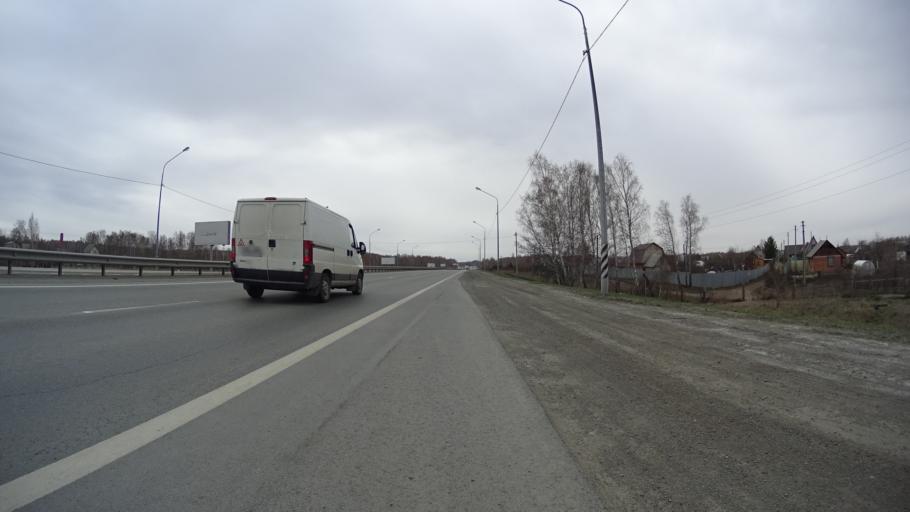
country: RU
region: Chelyabinsk
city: Novosineglazovskiy
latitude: 54.9792
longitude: 61.4148
